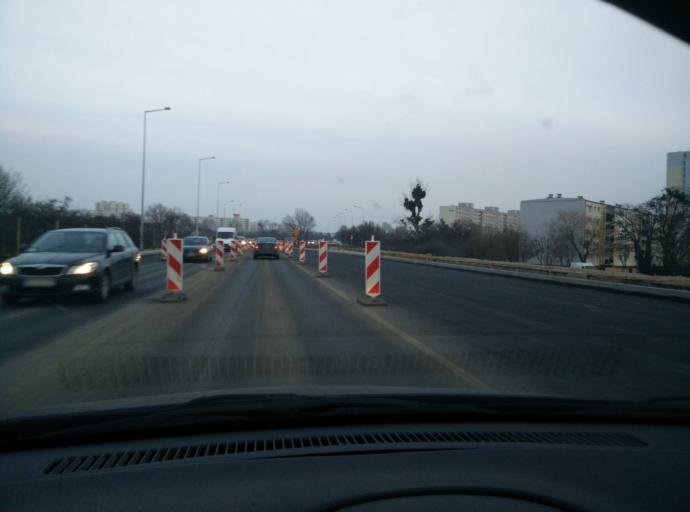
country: PL
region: Greater Poland Voivodeship
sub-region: Poznan
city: Poznan
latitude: 52.3933
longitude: 16.9582
